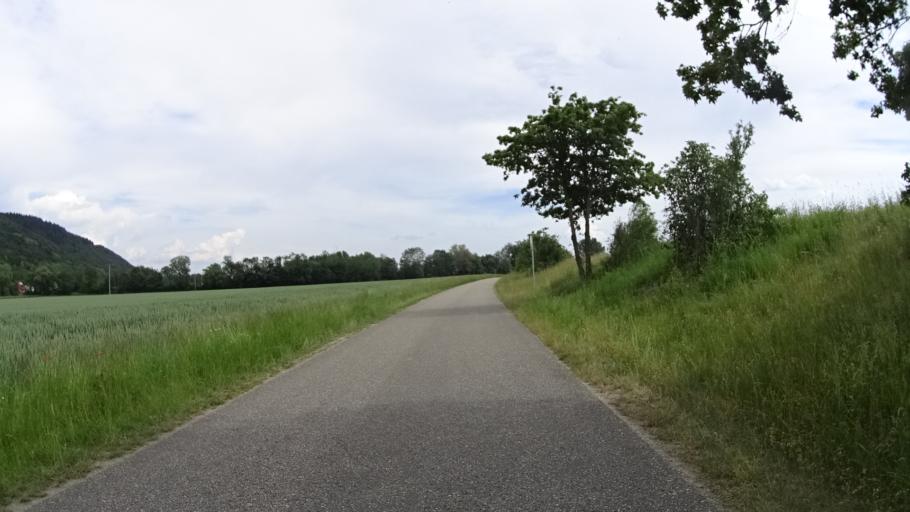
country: DE
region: Bavaria
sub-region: Upper Palatinate
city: Donaustauf
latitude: 49.0212
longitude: 12.2580
